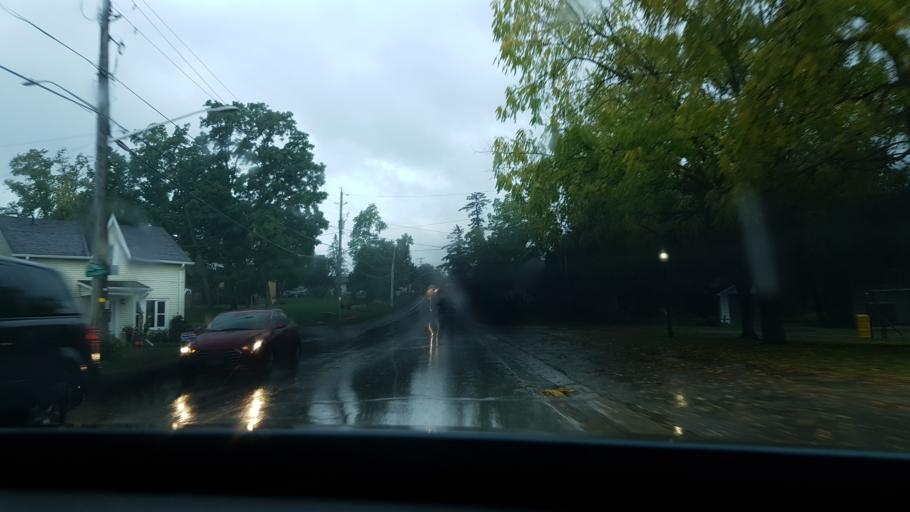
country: CA
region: Ontario
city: Peterborough
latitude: 44.3778
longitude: -78.3856
